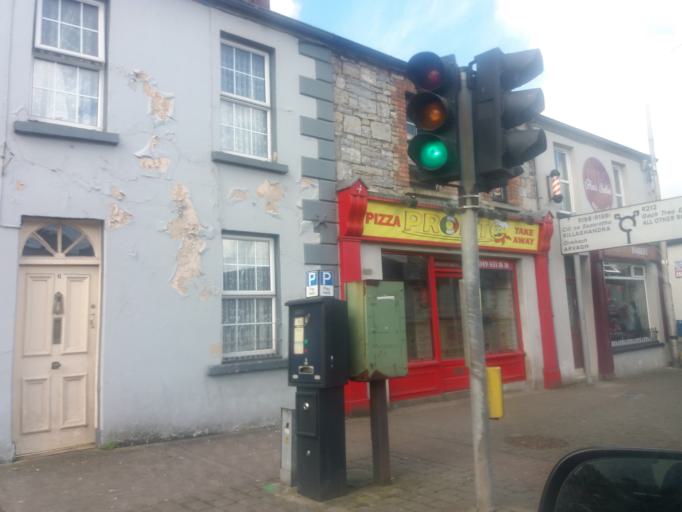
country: IE
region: Ulster
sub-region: An Cabhan
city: Cavan
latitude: 53.9892
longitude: -7.3629
